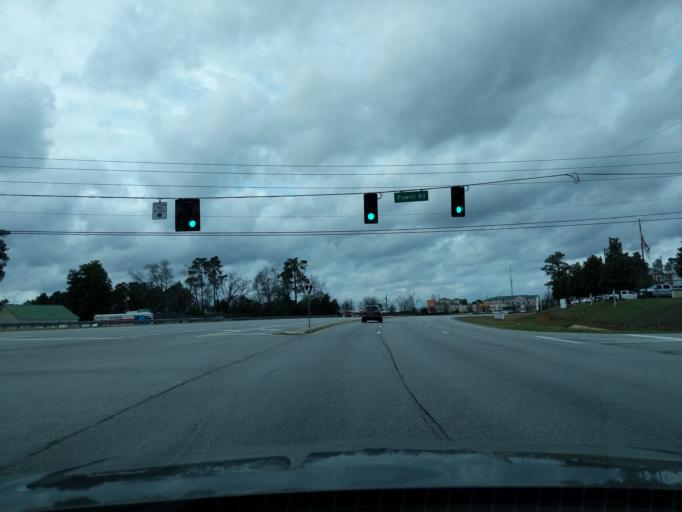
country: US
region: Georgia
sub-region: Columbia County
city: Evans
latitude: 33.4711
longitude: -82.1273
